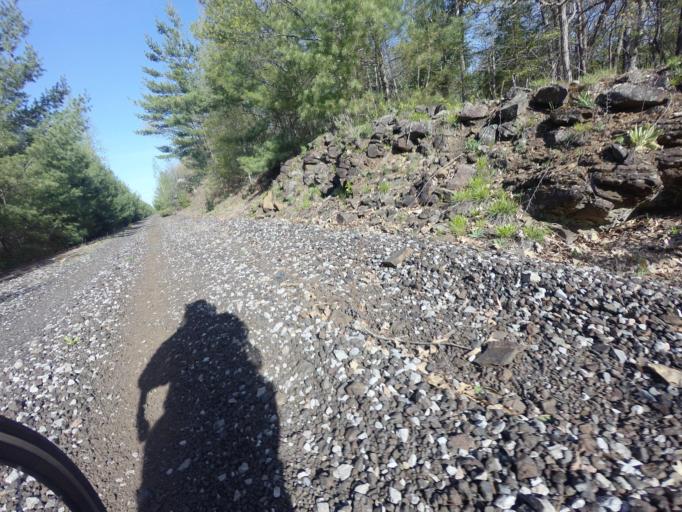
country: CA
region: Ontario
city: Arnprior
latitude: 45.4710
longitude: -76.3014
